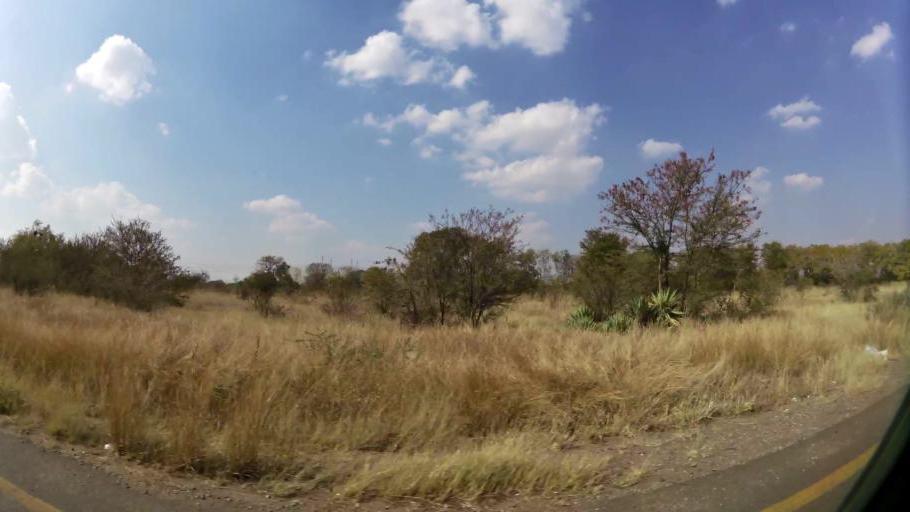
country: ZA
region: North-West
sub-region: Bojanala Platinum District Municipality
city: Mogwase
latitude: -25.4557
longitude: 27.0877
